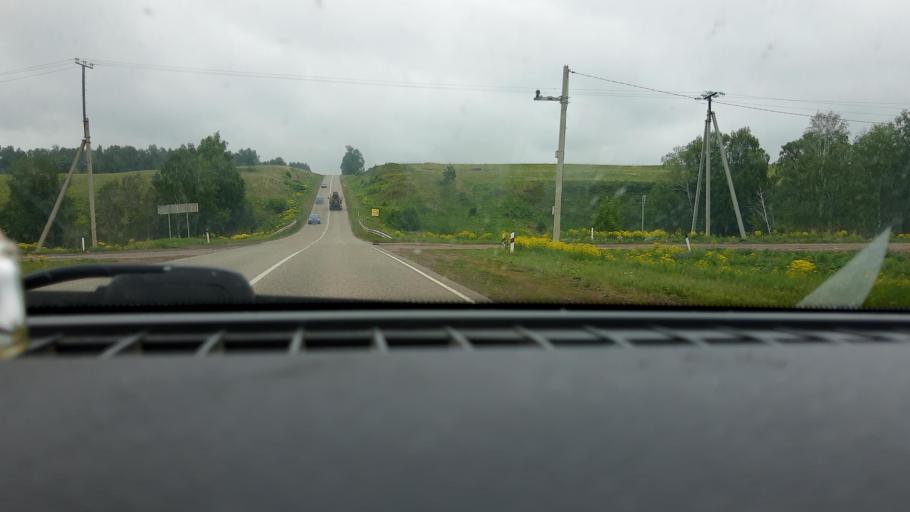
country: RU
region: Bashkortostan
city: Belebey
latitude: 54.0629
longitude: 54.0556
